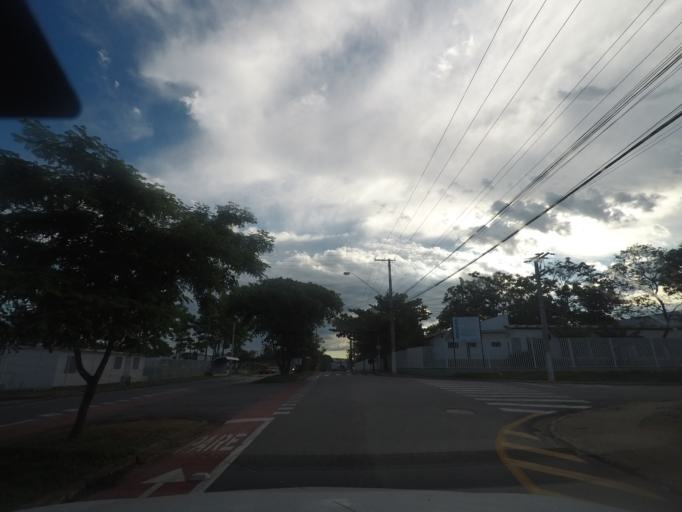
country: BR
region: Sao Paulo
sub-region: Taubate
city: Taubate
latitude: -23.0478
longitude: -45.5975
